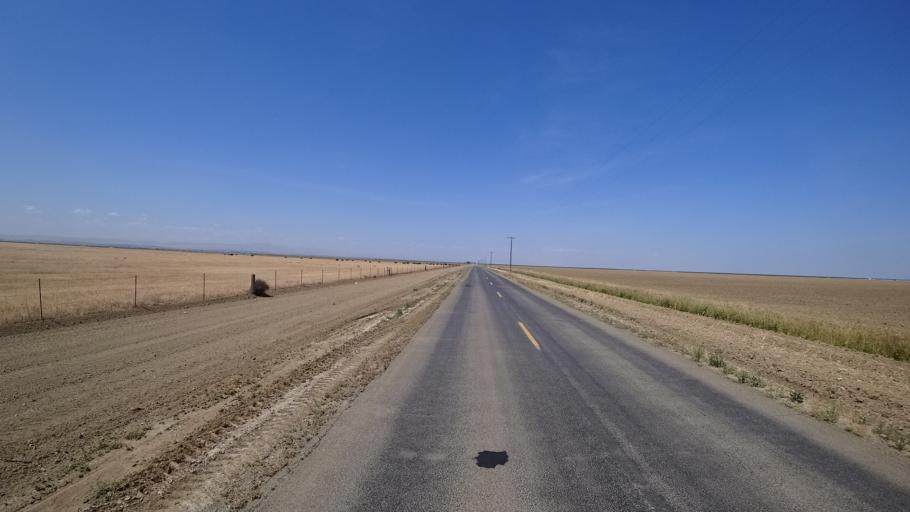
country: US
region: California
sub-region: Kings County
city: Stratford
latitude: 36.1377
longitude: -119.9283
